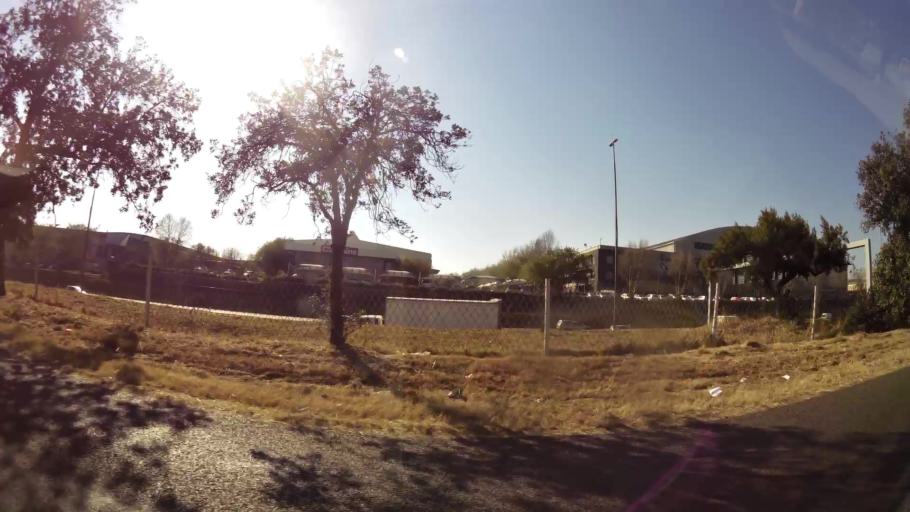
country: ZA
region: Gauteng
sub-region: City of Johannesburg Metropolitan Municipality
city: Modderfontein
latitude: -26.1124
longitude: 28.1307
